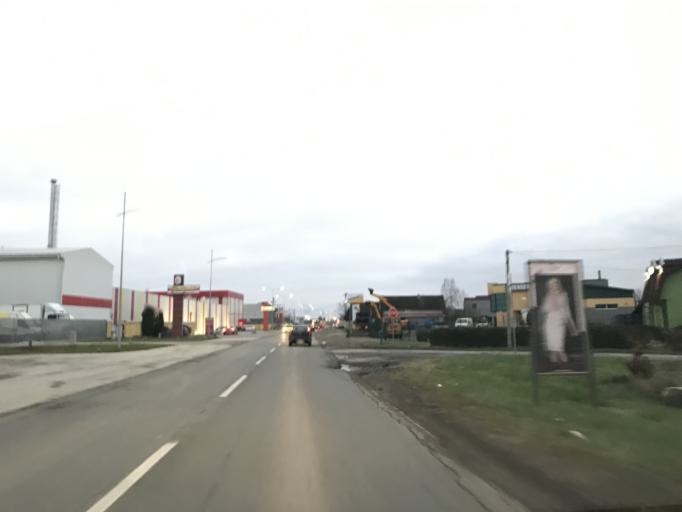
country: RS
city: Veternik
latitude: 45.2807
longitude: 19.7831
